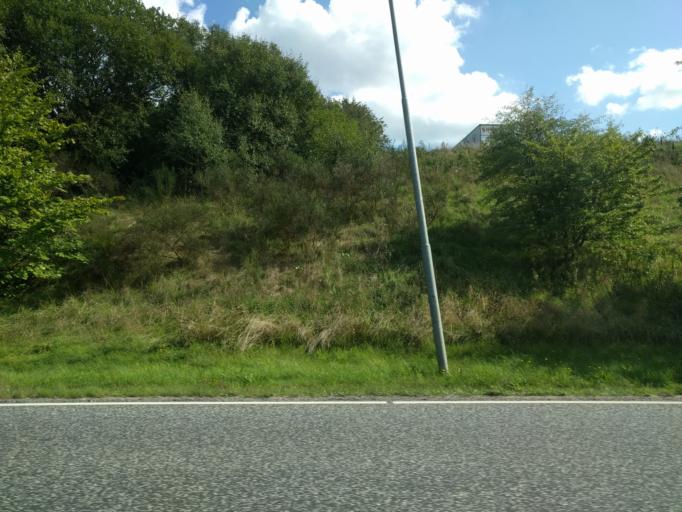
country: DK
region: Central Jutland
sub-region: Skive Kommune
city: Skive
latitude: 56.5839
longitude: 9.0287
